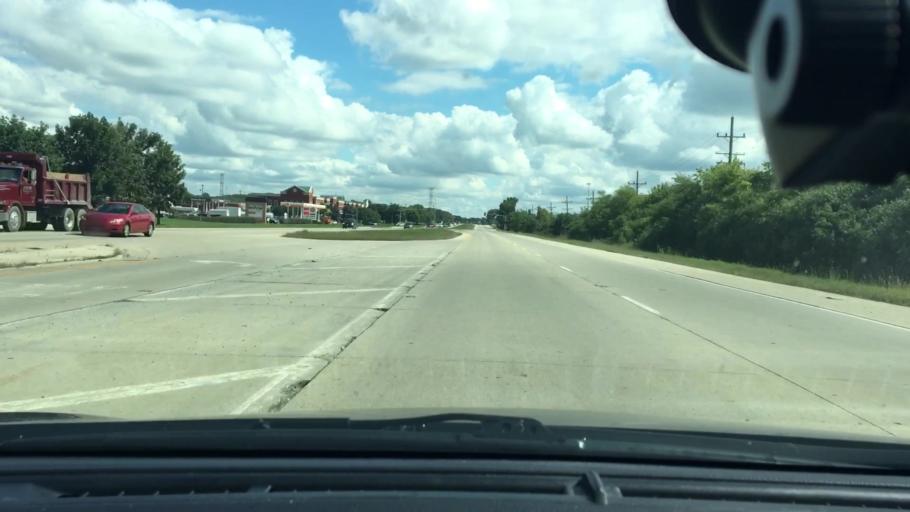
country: US
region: Illinois
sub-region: Kane County
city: East Dundee
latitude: 42.0893
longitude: -88.2483
